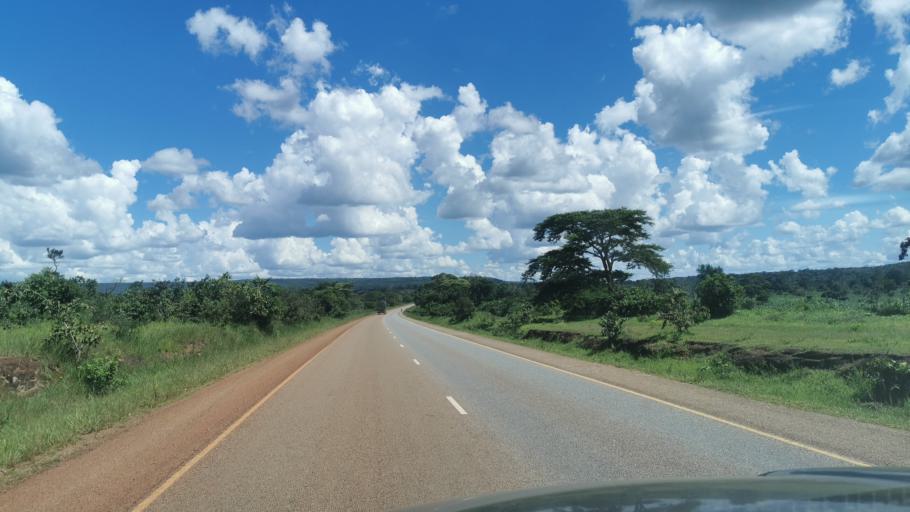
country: TZ
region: Geita
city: Uyovu
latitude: -3.0446
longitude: 31.2462
